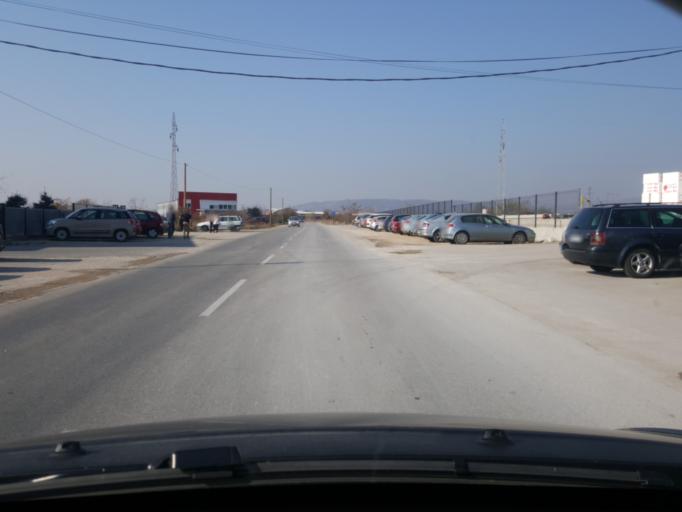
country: RS
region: Central Serbia
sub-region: Nisavski Okrug
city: Niska Banja
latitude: 43.3258
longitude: 21.9638
